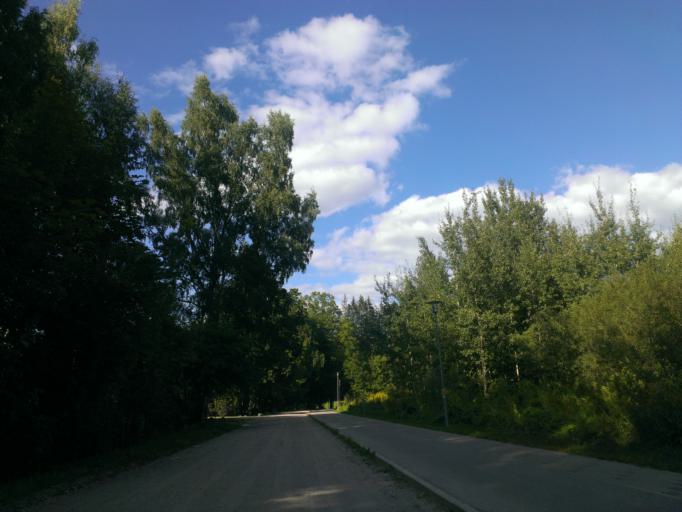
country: LV
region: Sigulda
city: Sigulda
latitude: 57.1689
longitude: 24.8715
